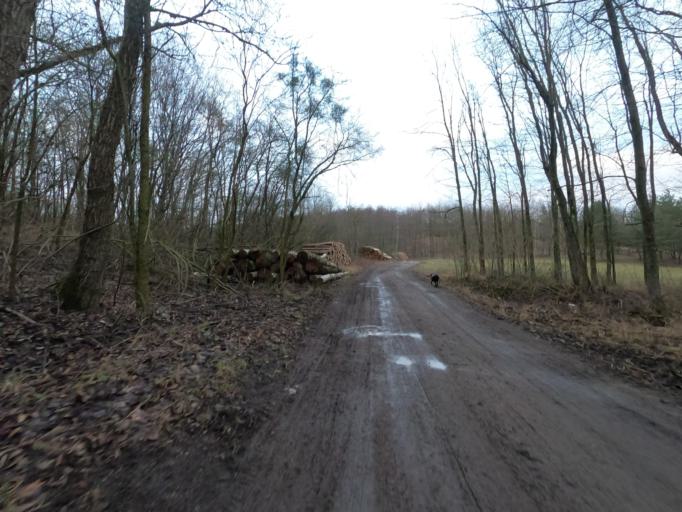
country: PL
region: Greater Poland Voivodeship
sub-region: Powiat pilski
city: Wyrzysk
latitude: 53.1162
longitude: 17.2084
